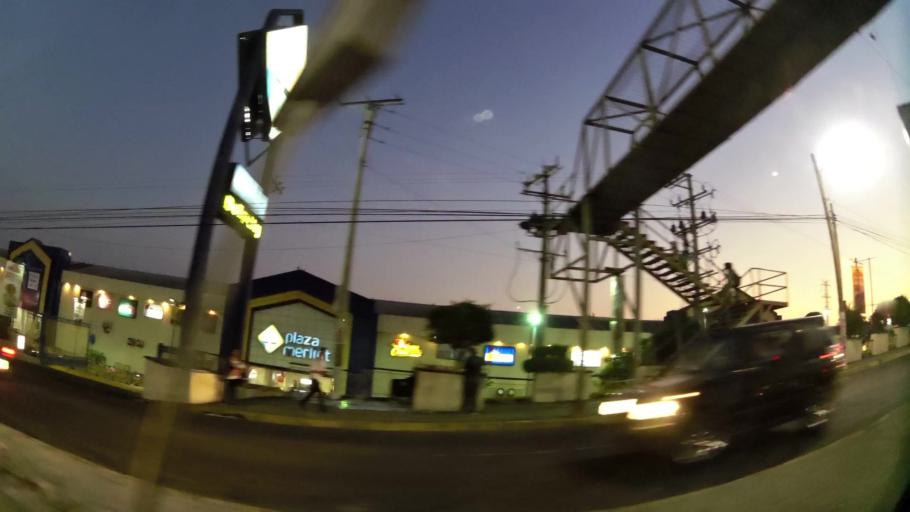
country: SV
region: La Libertad
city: Santa Tecla
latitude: 13.6795
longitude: -89.2758
